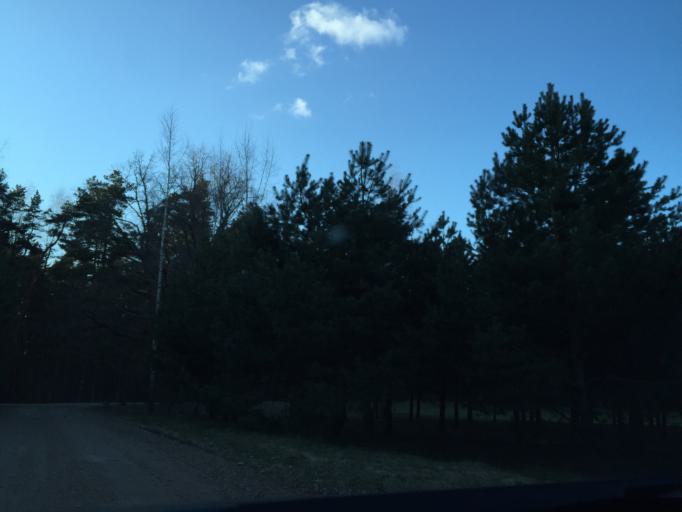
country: LV
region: Kekava
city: Kekava
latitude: 56.8538
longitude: 24.2331
